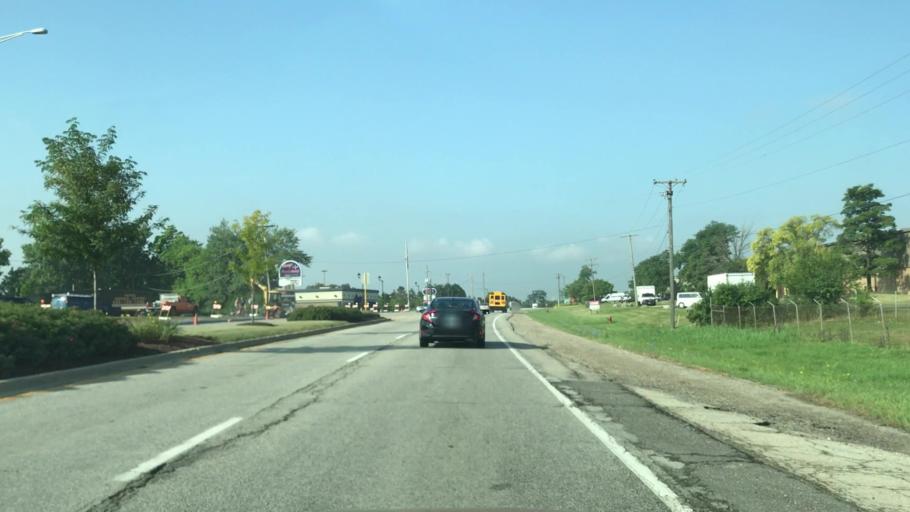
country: US
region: Illinois
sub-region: Will County
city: Romeoville
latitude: 41.6665
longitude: -88.0666
